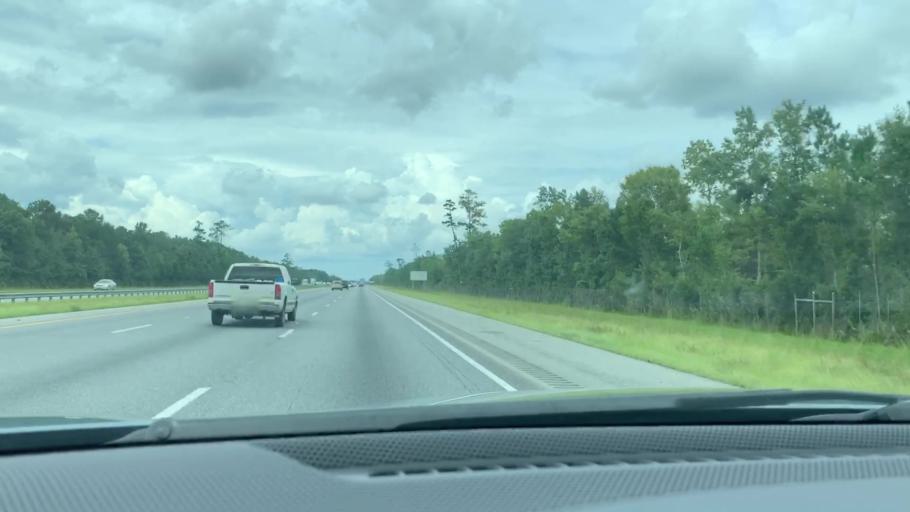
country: US
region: Georgia
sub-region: McIntosh County
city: Darien
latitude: 31.4488
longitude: -81.4449
